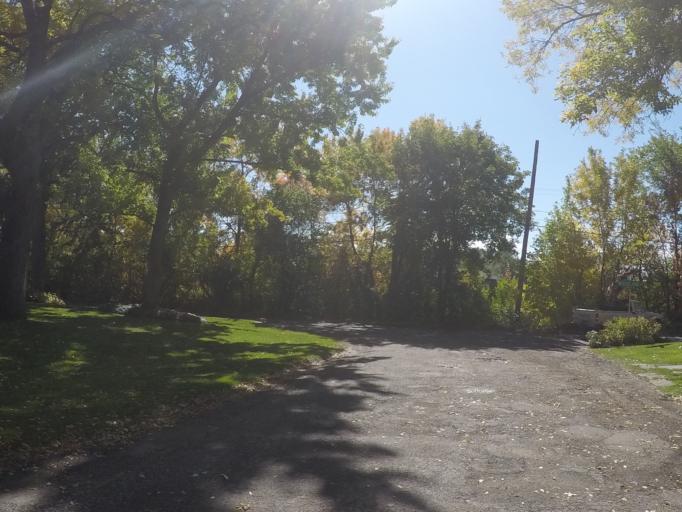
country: US
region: Montana
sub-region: Yellowstone County
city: Billings
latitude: 45.7955
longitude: -108.5296
